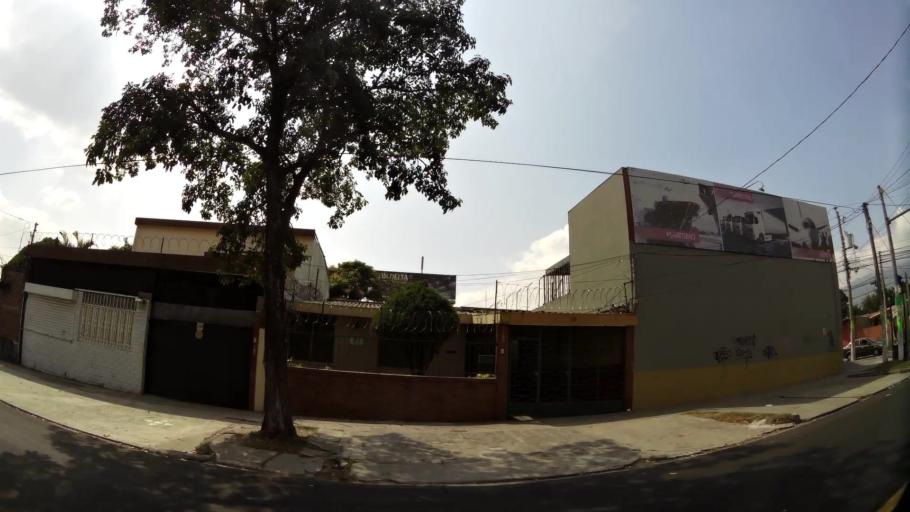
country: SV
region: San Salvador
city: Mejicanos
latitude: 13.7127
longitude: -89.2174
